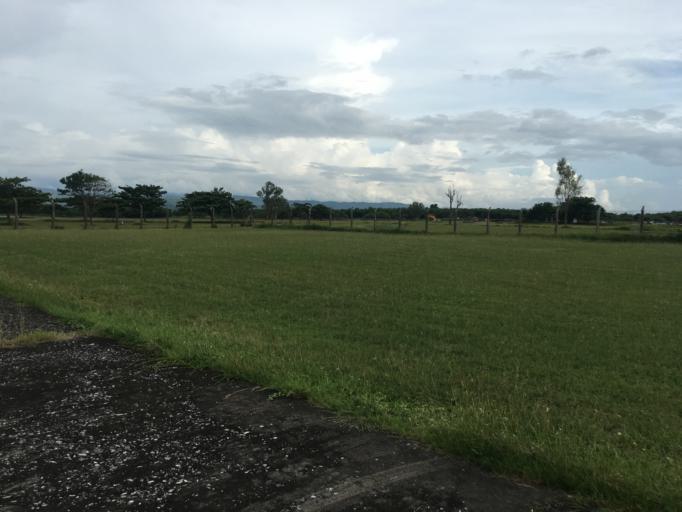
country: PH
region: Ilocos
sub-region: Province of La Union
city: San Fernando
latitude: 16.6188
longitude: 120.2791
